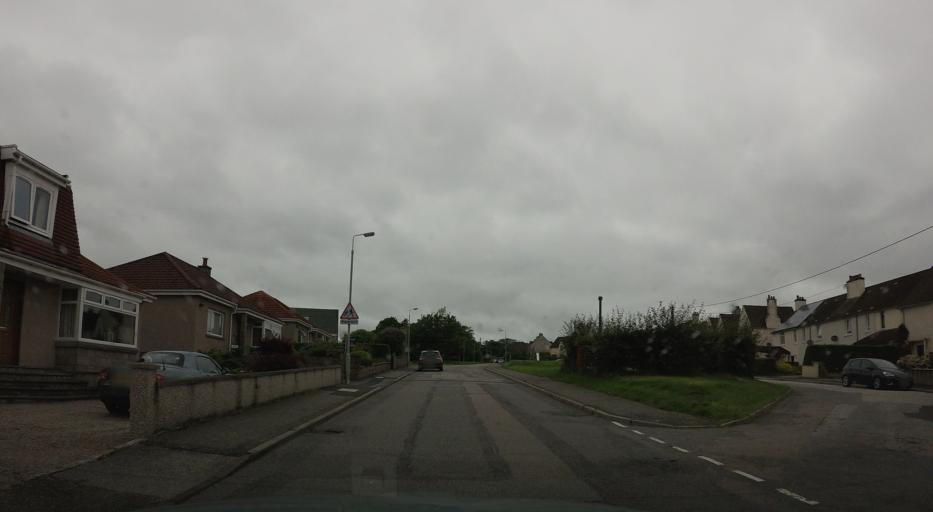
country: GB
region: Scotland
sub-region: Aberdeenshire
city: Banchory
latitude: 57.0556
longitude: -2.4928
